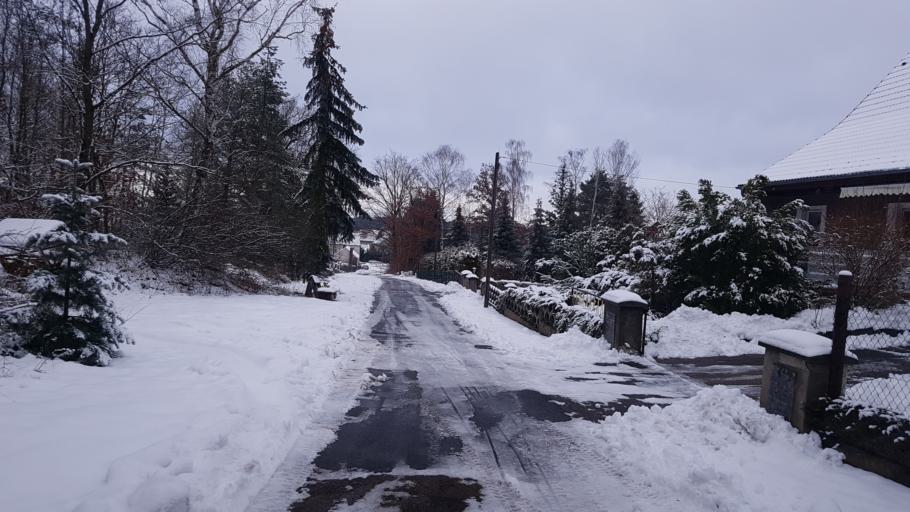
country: DE
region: Brandenburg
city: Crinitz
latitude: 51.7354
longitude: 13.7670
